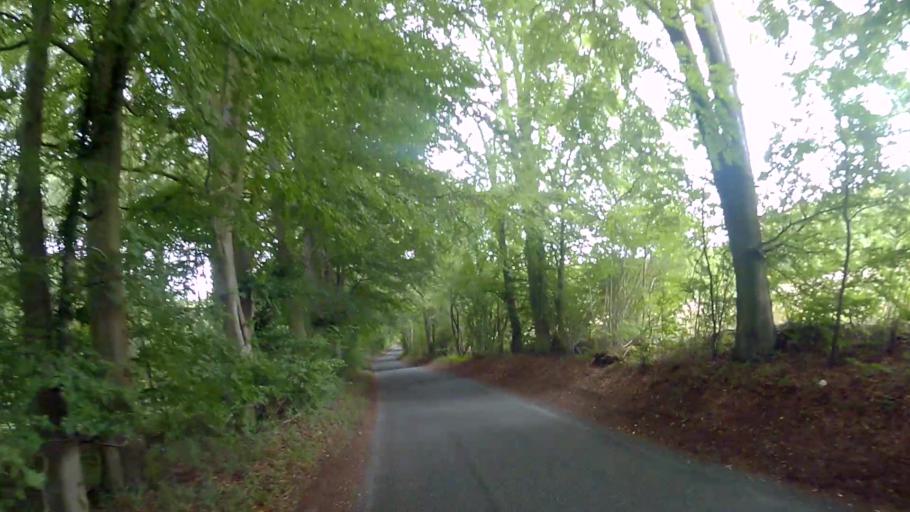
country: GB
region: England
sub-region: Hampshire
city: Overton
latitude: 51.1928
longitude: -1.2795
